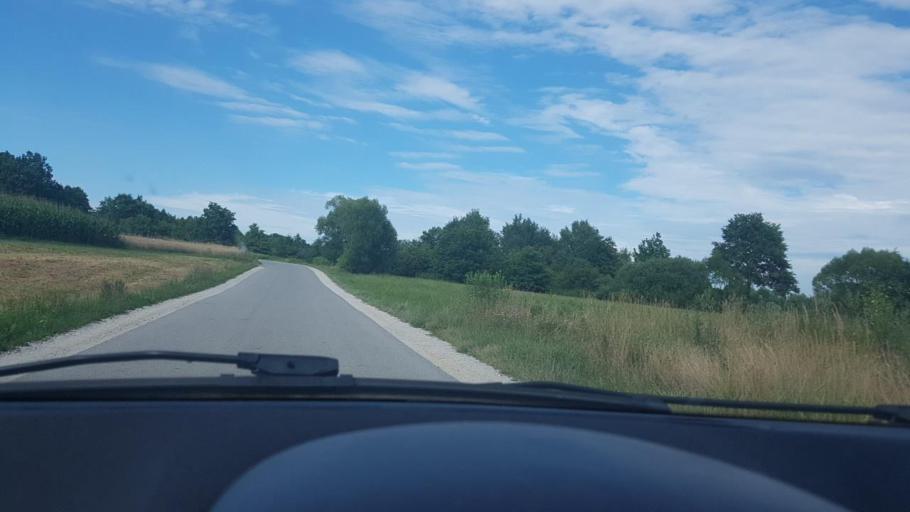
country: HR
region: Varazdinska
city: Tuzno
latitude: 46.2662
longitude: 16.1915
